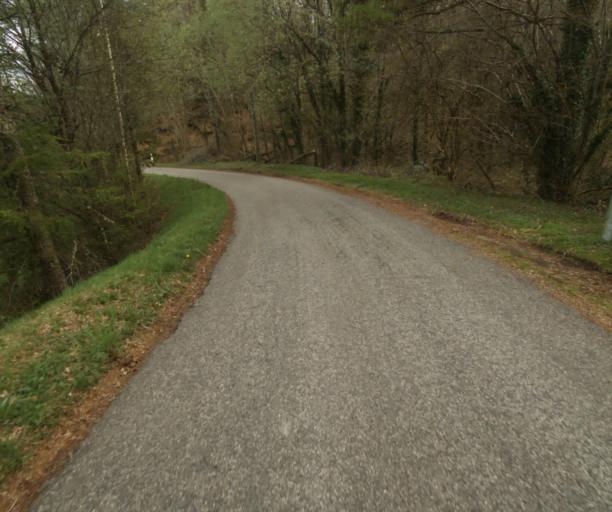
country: FR
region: Limousin
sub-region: Departement de la Correze
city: Argentat
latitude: 45.1985
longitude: 1.9348
